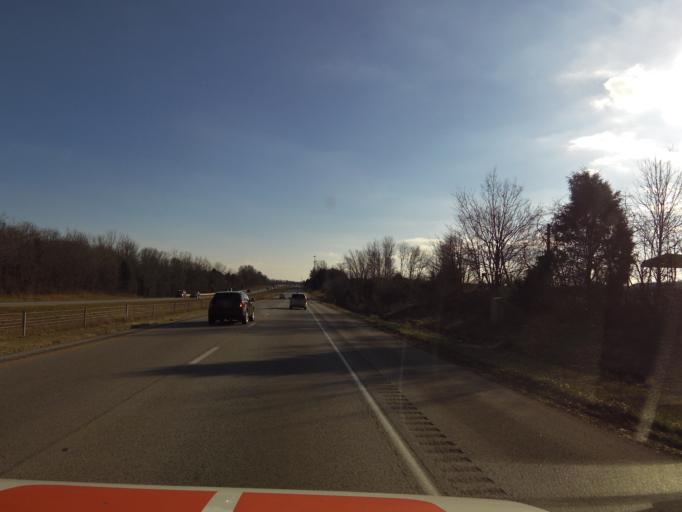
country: US
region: Indiana
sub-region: Clark County
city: Sellersburg
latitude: 38.4507
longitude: -85.7694
